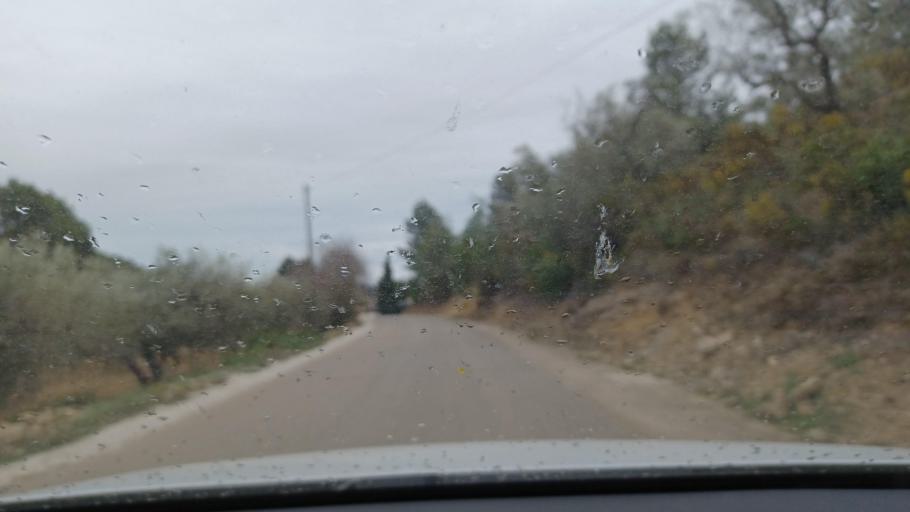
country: ES
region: Valencia
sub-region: Provincia de Castello
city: Traiguera
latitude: 40.5044
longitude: 0.2974
